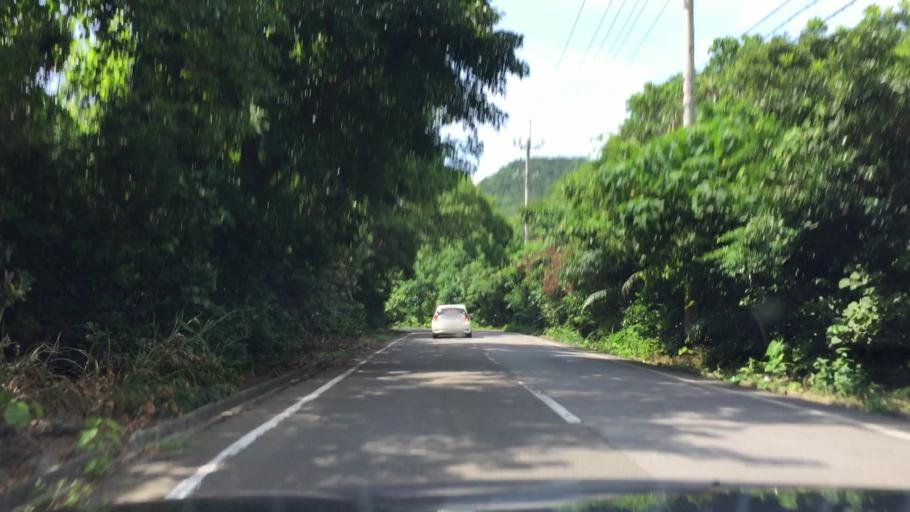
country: JP
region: Okinawa
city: Ishigaki
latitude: 24.4643
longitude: 124.2268
